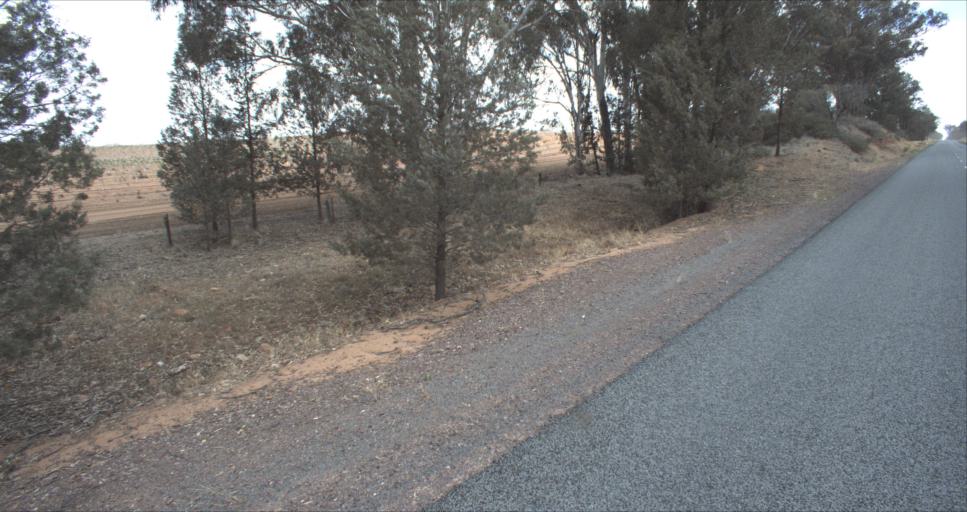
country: AU
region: New South Wales
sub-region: Leeton
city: Leeton
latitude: -34.6548
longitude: 146.3505
